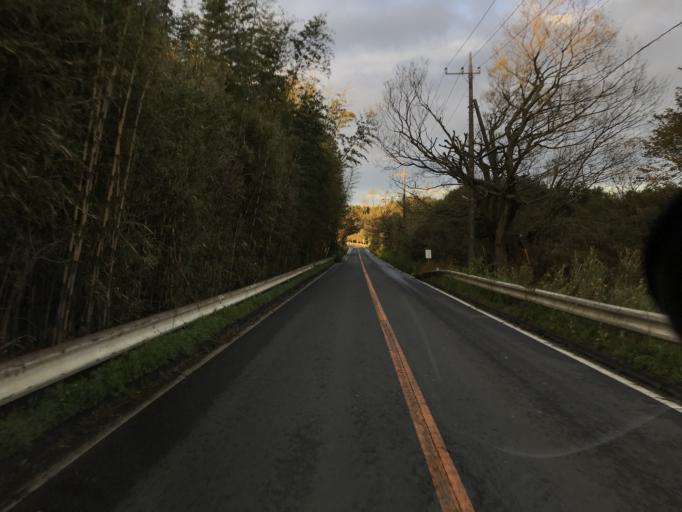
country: JP
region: Chiba
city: Sawara
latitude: 35.8113
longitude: 140.4518
